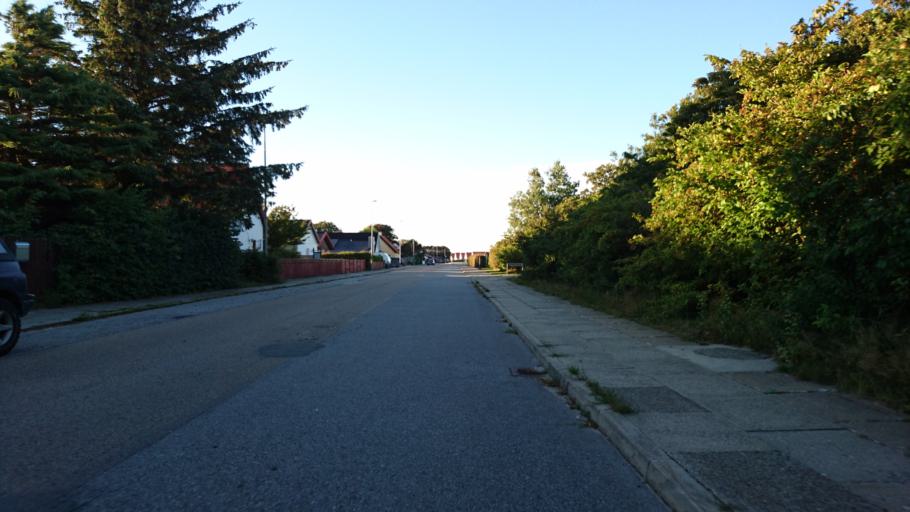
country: DK
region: North Denmark
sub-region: Frederikshavn Kommune
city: Skagen
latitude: 57.7287
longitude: 10.5829
